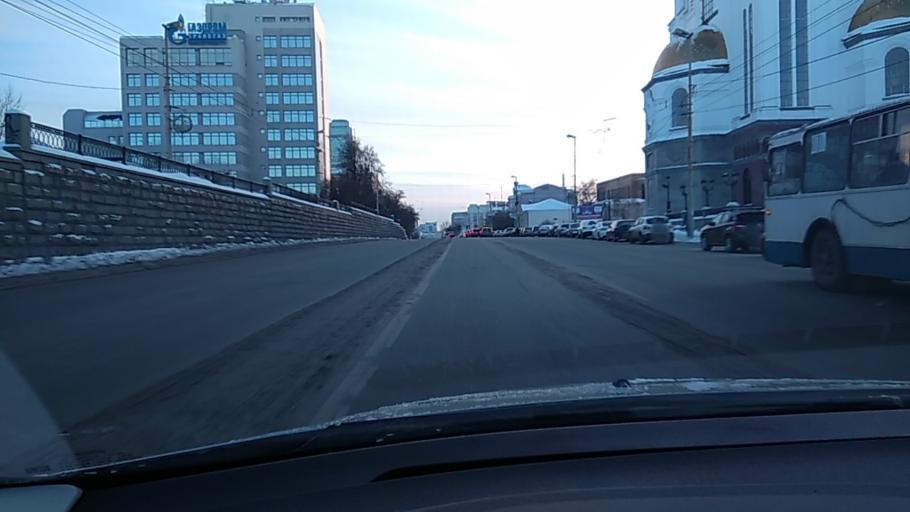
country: RU
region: Sverdlovsk
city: Yekaterinburg
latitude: 56.8452
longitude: 60.6095
